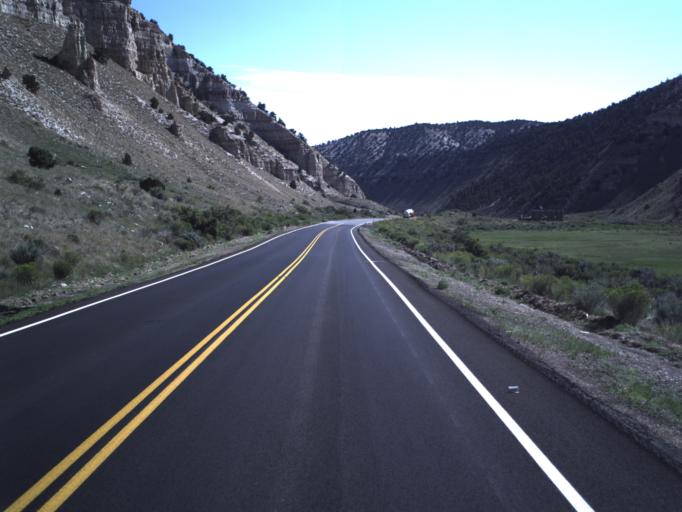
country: US
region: Utah
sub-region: Duchesne County
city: Duchesne
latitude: 40.0284
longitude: -110.5505
